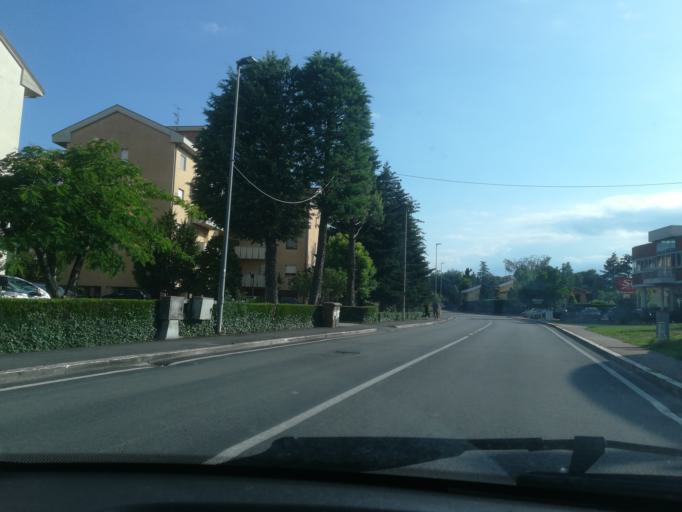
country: IT
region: The Marches
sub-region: Provincia di Macerata
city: Villa Potenza
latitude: 43.3198
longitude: 13.4233
